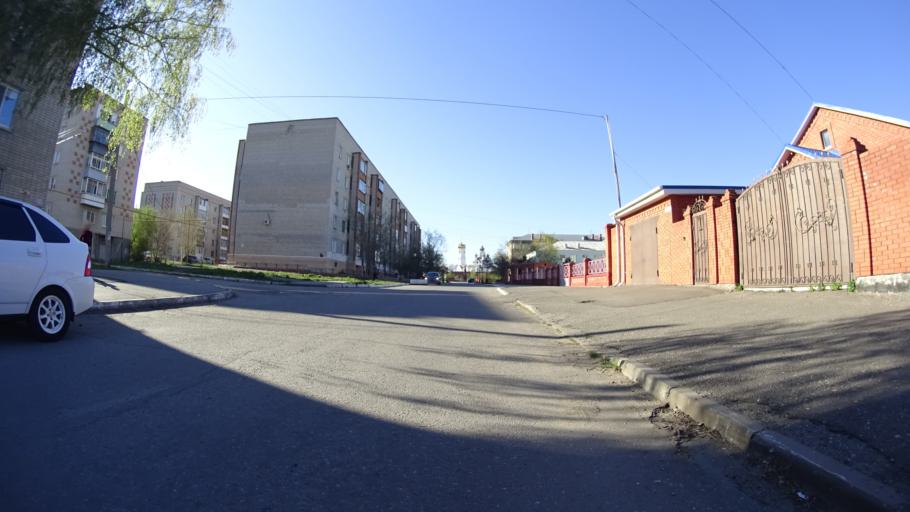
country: RU
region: Chelyabinsk
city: Troitsk
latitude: 54.0821
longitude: 61.5428
